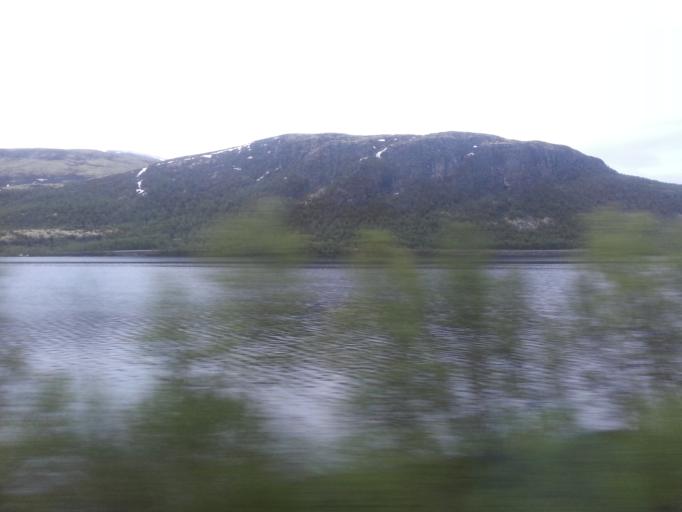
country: NO
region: Oppland
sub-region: Dovre
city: Dovre
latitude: 62.1774
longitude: 9.4026
